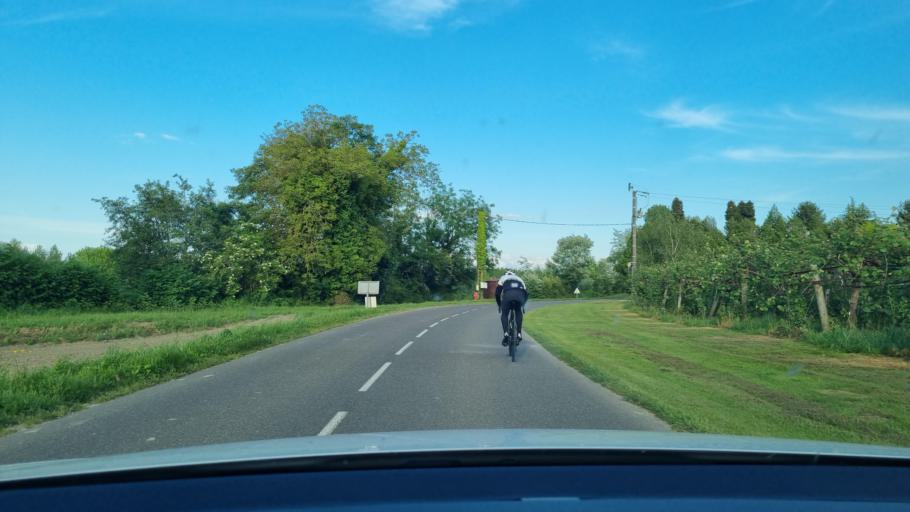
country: FR
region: Aquitaine
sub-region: Departement des Landes
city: Peyrehorade
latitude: 43.5415
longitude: -1.1309
